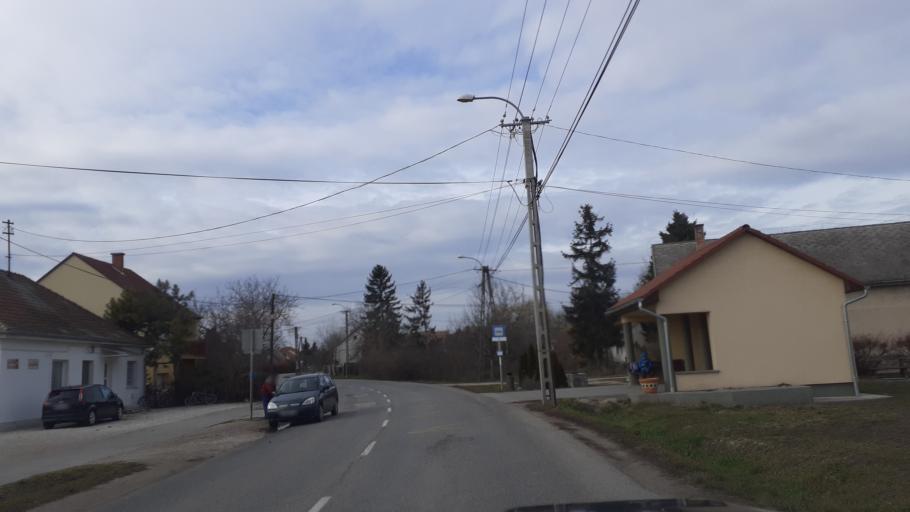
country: HU
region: Fejer
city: Szabadbattyan
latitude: 47.0809
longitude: 18.4102
